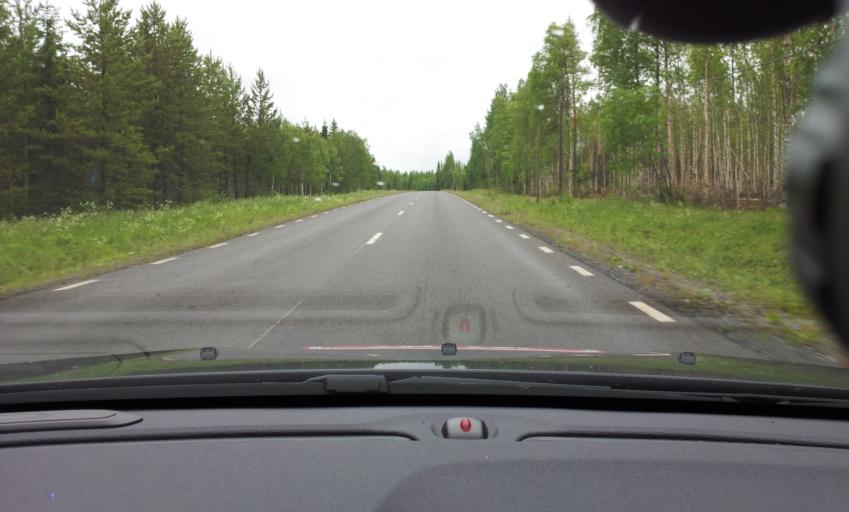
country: SE
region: Jaemtland
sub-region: OEstersunds Kommun
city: Lit
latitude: 63.7005
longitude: 14.9931
